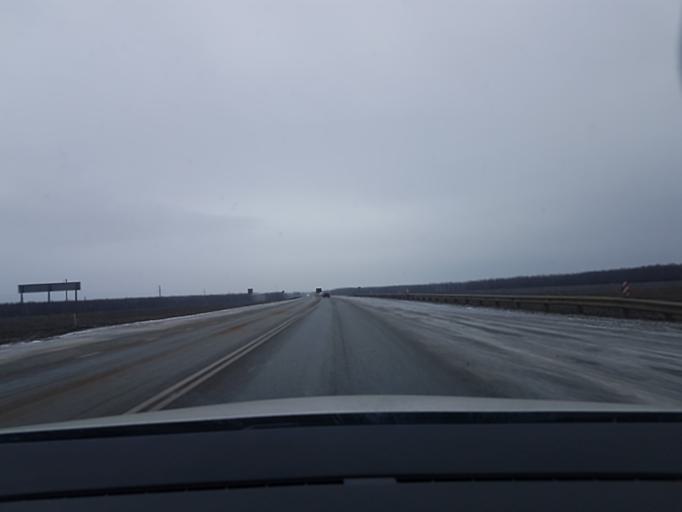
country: RU
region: Tambov
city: Zavoronezhskoye
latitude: 52.9890
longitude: 40.5574
